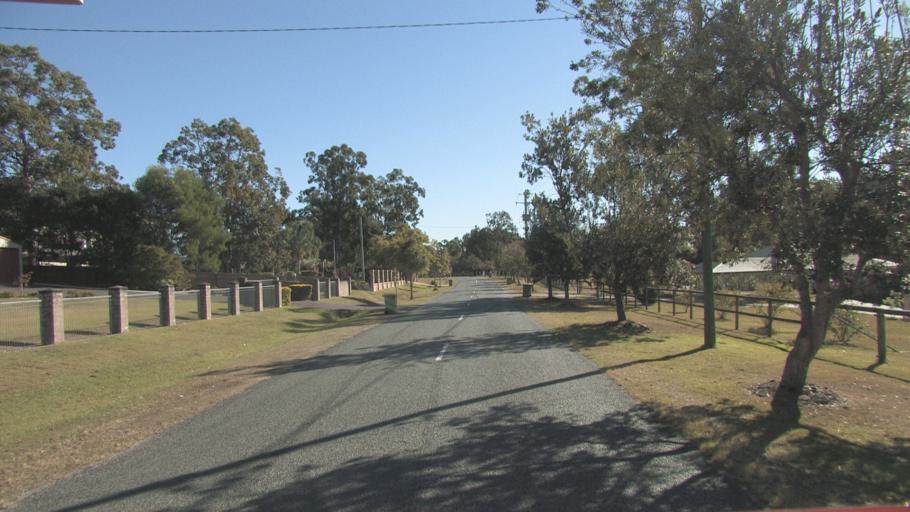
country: AU
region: Queensland
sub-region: Logan
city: North Maclean
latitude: -27.7459
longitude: 152.9556
